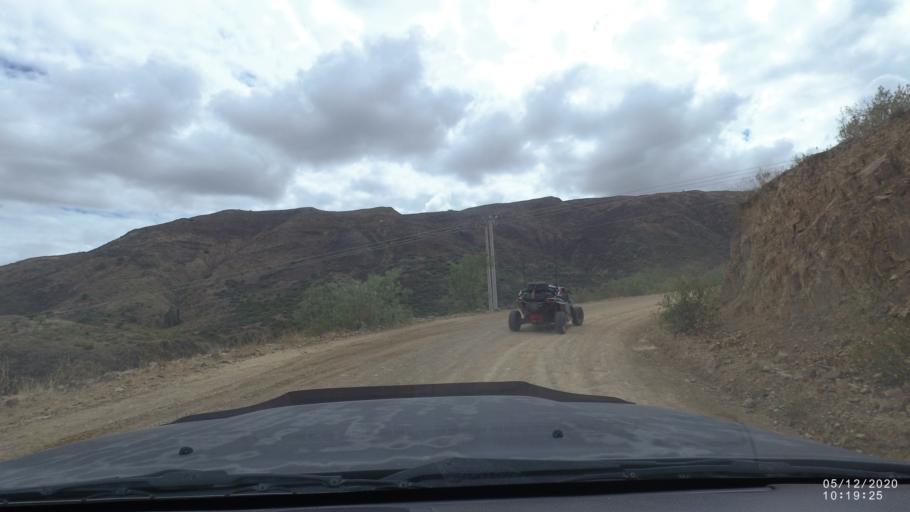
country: BO
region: Cochabamba
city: Sipe Sipe
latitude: -17.4791
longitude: -66.2836
